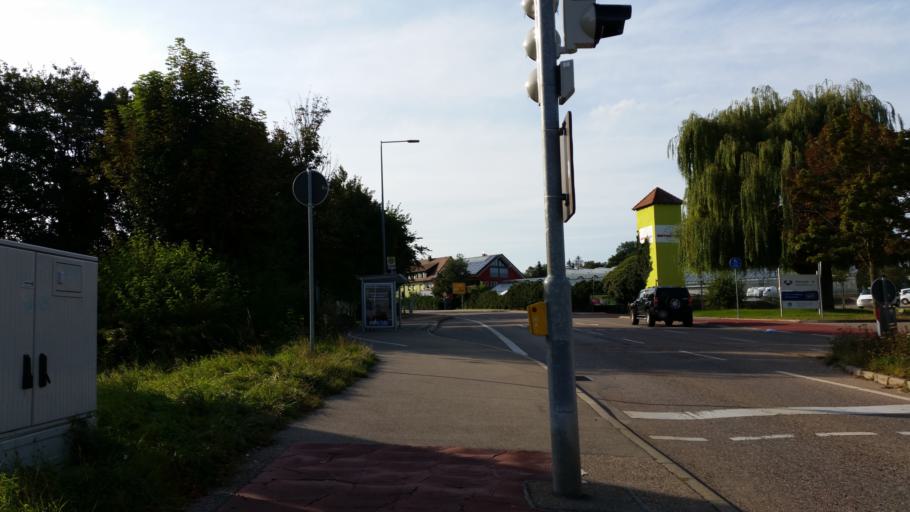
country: DE
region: Baden-Wuerttemberg
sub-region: Regierungsbezirk Stuttgart
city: Ludwigsburg
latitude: 48.8804
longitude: 9.2185
